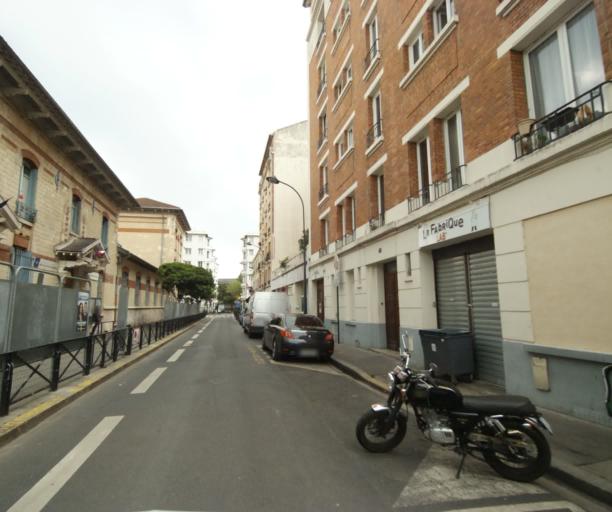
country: FR
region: Ile-de-France
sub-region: Departement des Hauts-de-Seine
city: Clichy
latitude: 48.9016
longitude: 2.2996
